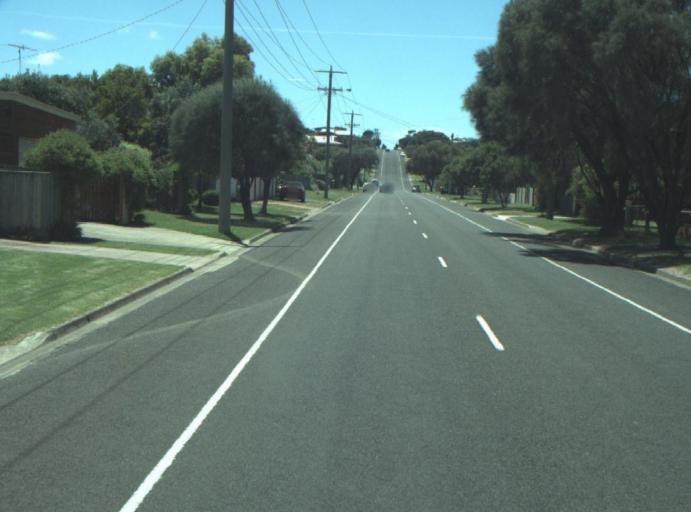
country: AU
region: Victoria
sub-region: Greater Geelong
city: Clifton Springs
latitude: -38.2645
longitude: 144.5534
